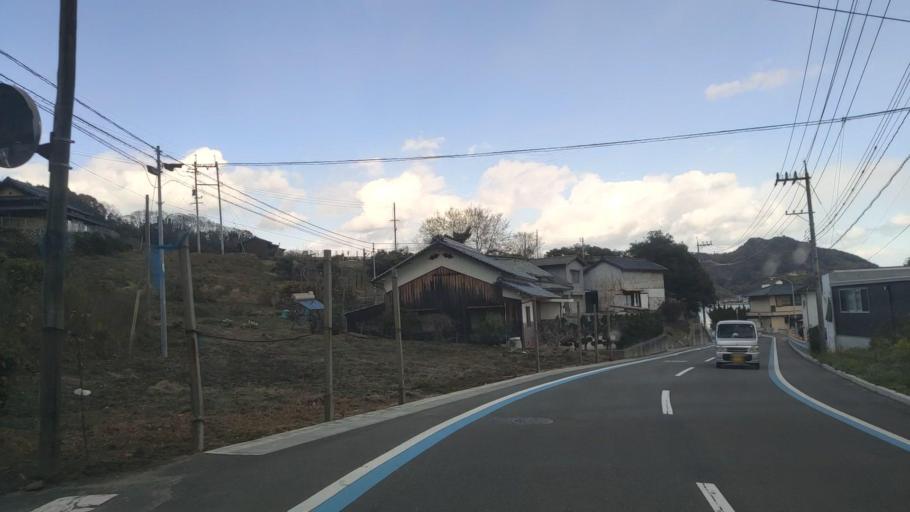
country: JP
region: Hiroshima
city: Innoshima
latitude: 34.1989
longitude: 133.0884
